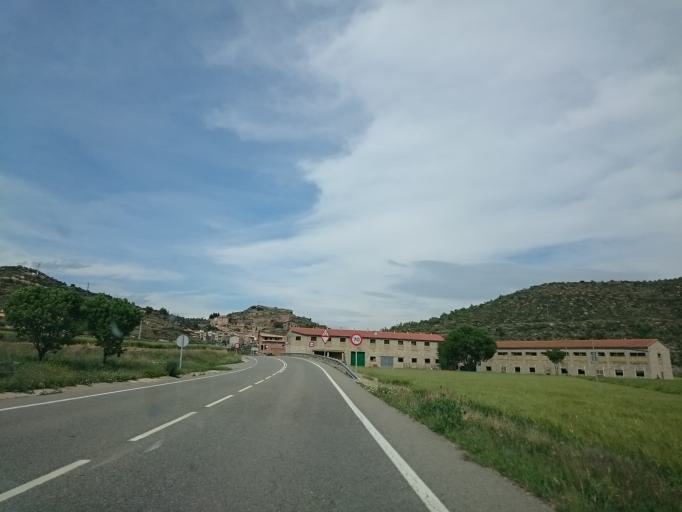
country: ES
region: Catalonia
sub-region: Provincia de Lleida
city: Tora de Riubregos
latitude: 41.8369
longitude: 1.3541
